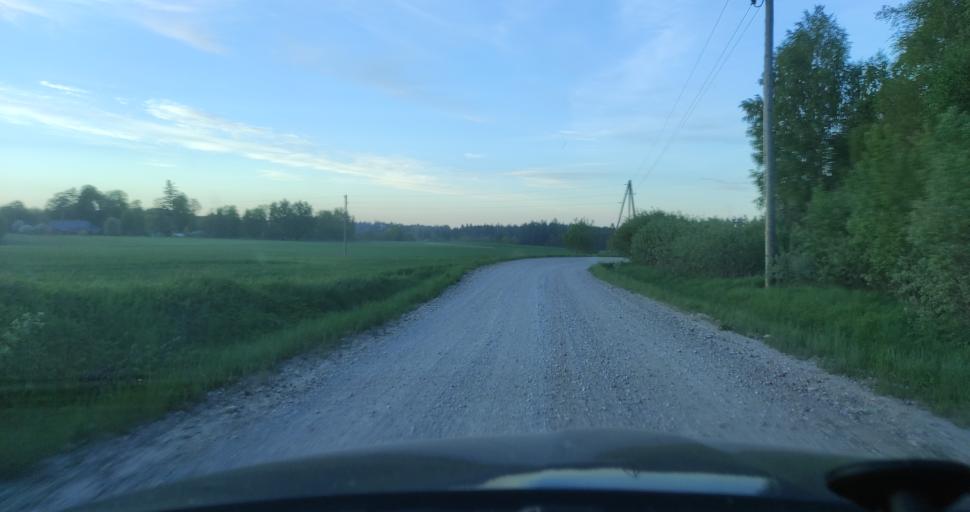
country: LV
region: Kuldigas Rajons
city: Kuldiga
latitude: 56.9523
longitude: 21.9182
